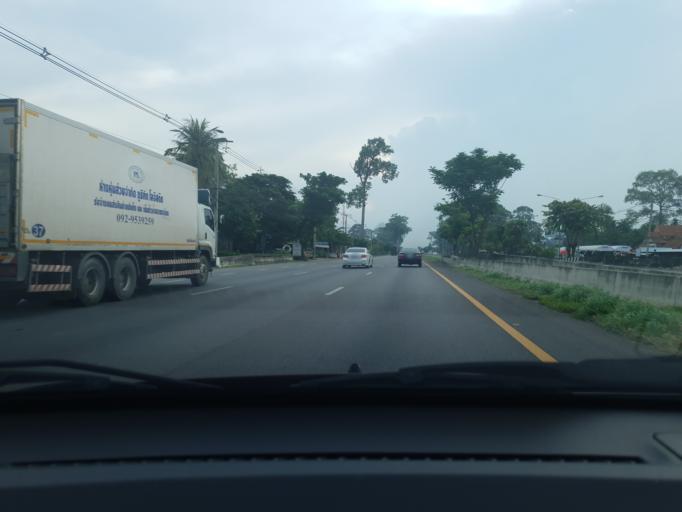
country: TH
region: Phetchaburi
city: Ban Lat
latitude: 13.0167
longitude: 99.9197
